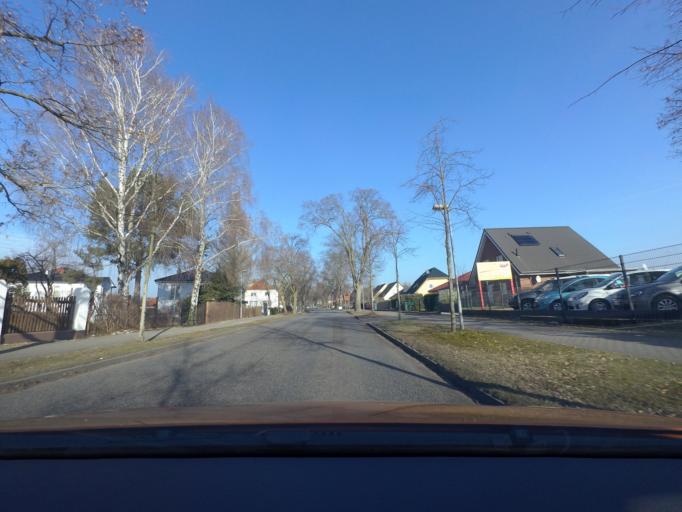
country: DE
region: Berlin
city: Blankenfelde
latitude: 52.6401
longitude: 13.3761
